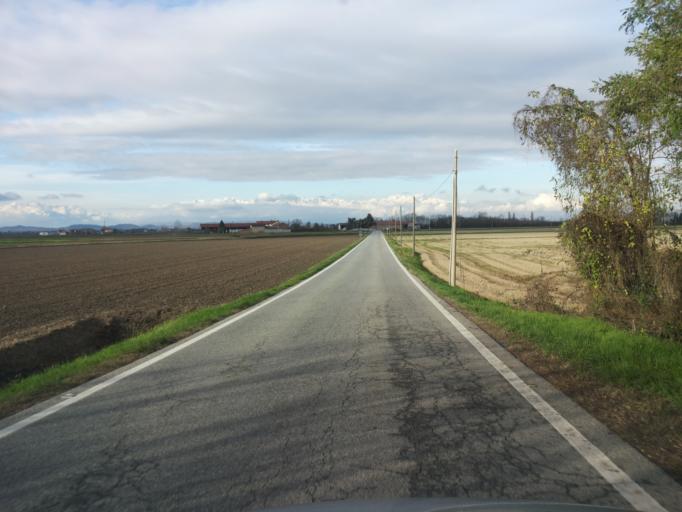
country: IT
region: Piedmont
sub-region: Provincia di Vercelli
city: Crova
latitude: 45.3217
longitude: 8.1947
